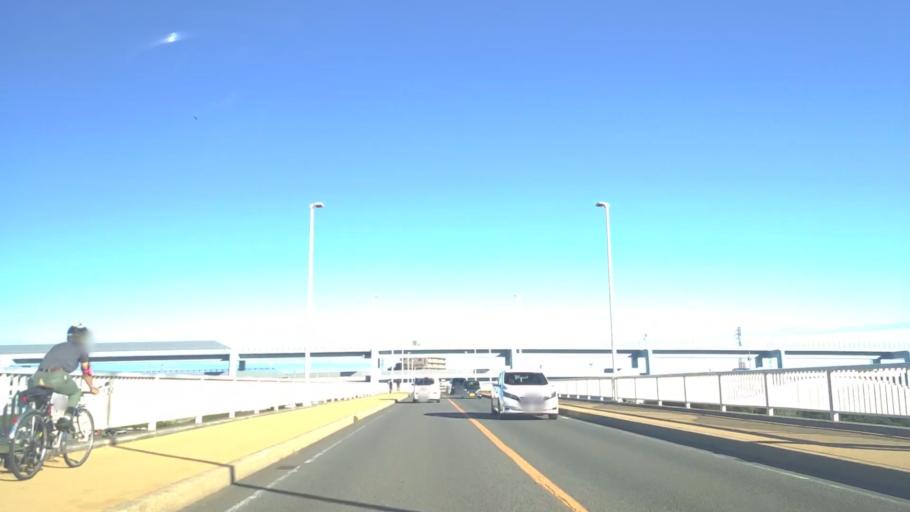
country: JP
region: Kanagawa
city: Chigasaki
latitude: 35.3736
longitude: 139.3717
